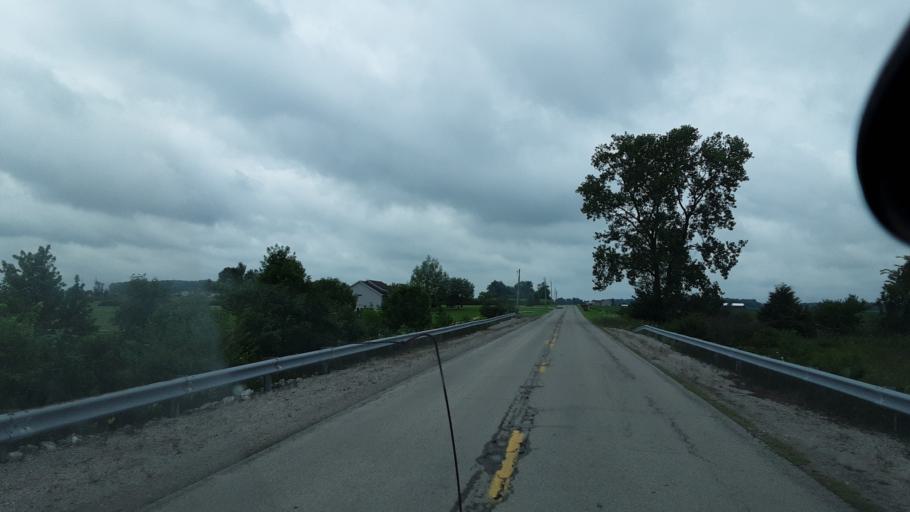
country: US
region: Indiana
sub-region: Wells County
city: Ossian
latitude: 40.9322
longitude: -85.1042
